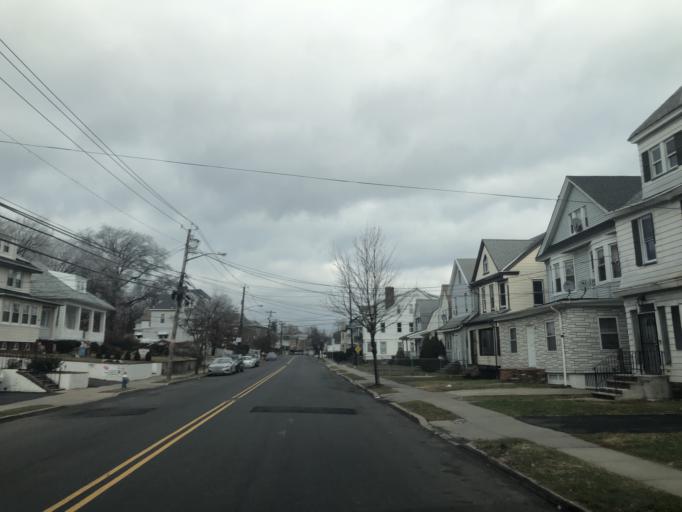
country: US
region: New Jersey
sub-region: Essex County
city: Irvington
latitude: 40.7312
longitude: -74.2354
